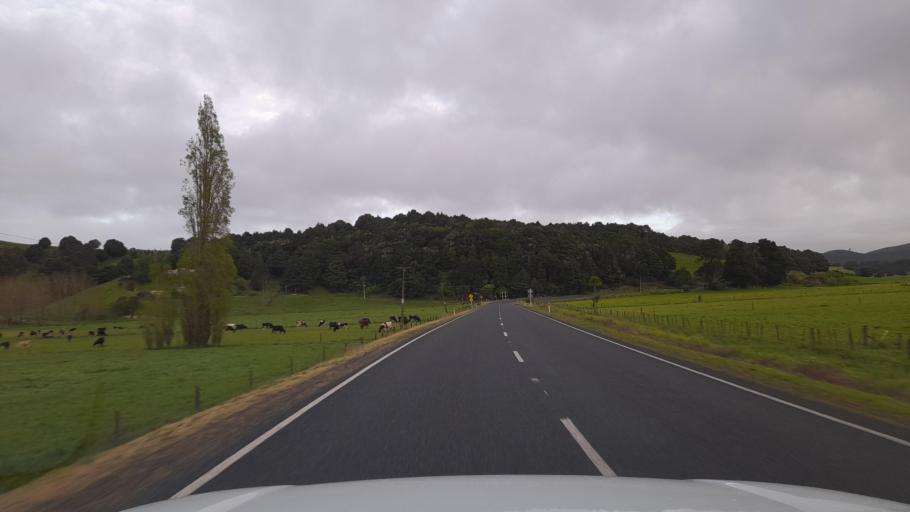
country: NZ
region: Northland
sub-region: Whangarei
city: Maungatapere
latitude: -35.7192
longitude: 174.0315
